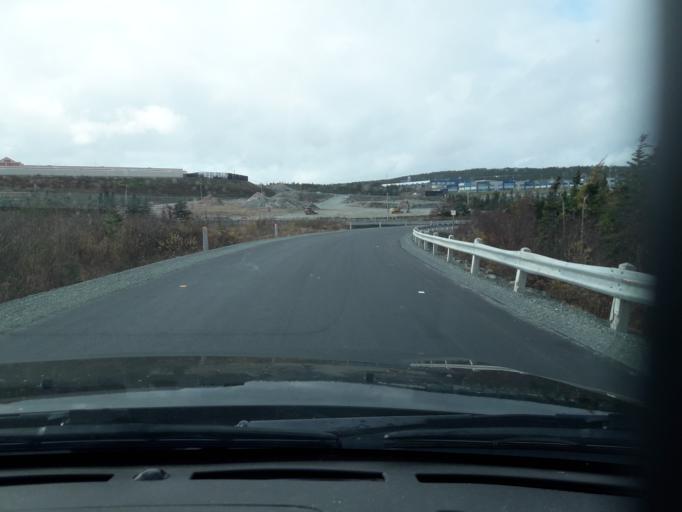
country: CA
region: Newfoundland and Labrador
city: Mount Pearl
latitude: 47.5561
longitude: -52.7754
